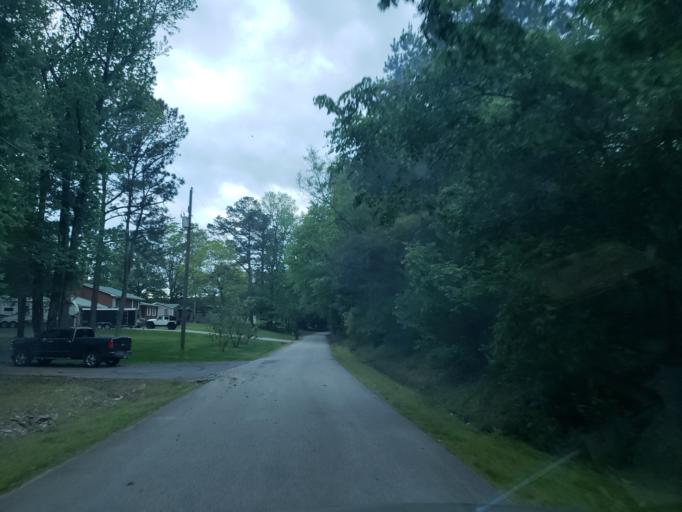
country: US
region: Georgia
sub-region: Paulding County
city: Hiram
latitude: 33.9027
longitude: -84.7269
